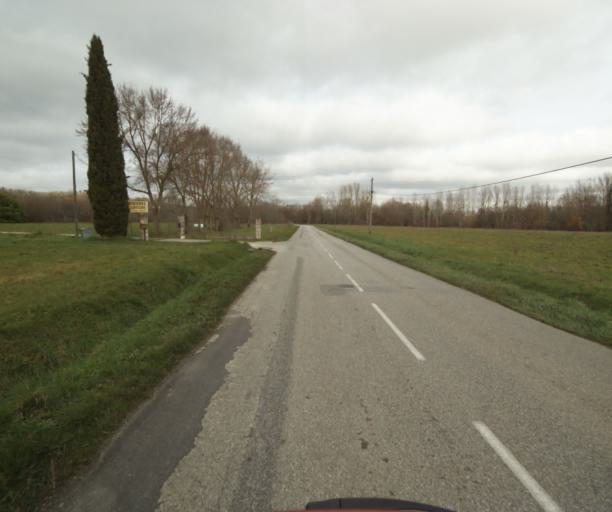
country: FR
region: Midi-Pyrenees
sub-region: Departement de l'Ariege
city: Pamiers
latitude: 43.1387
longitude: 1.5949
